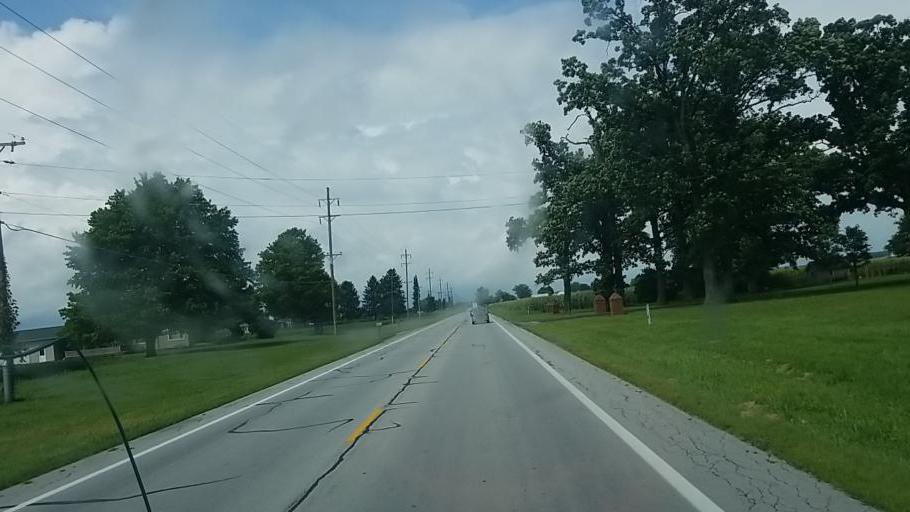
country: US
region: Ohio
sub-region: Logan County
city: West Liberty
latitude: 40.1852
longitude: -83.7424
